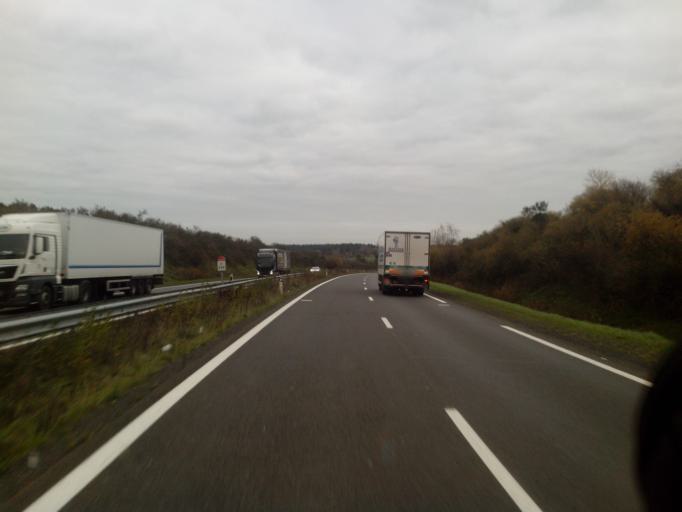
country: FR
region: Pays de la Loire
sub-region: Departement de la Loire-Atlantique
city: La Regrippiere
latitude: 47.1546
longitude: -1.2049
